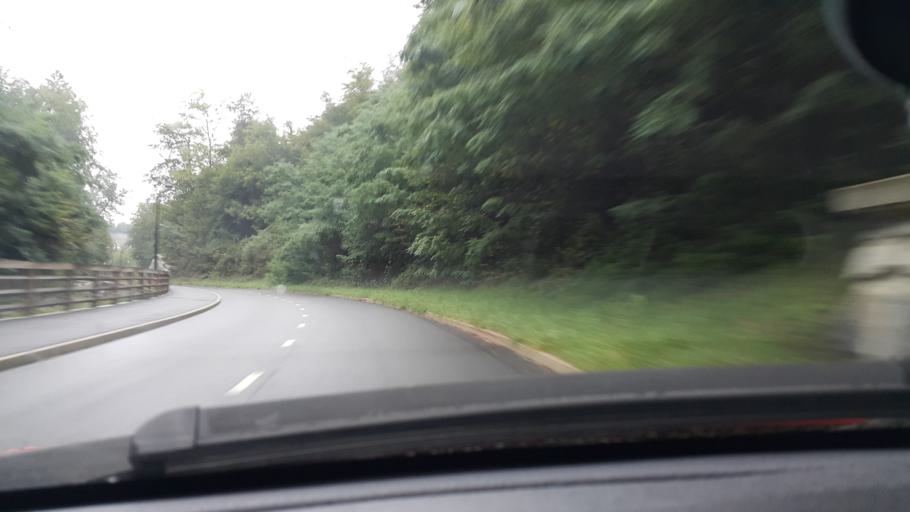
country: SI
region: Maribor
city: Maribor
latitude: 46.5688
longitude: 15.6445
